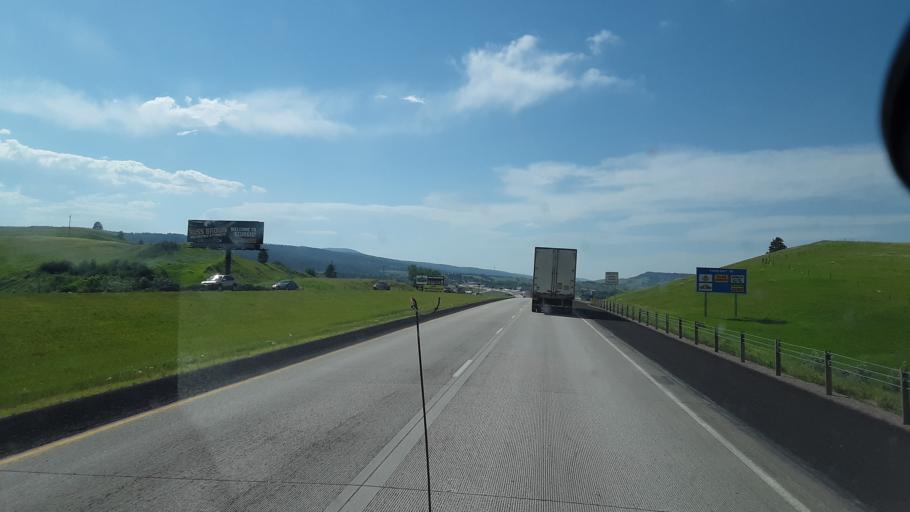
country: US
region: South Dakota
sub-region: Meade County
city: Sturgis
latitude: 44.3891
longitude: -103.4904
